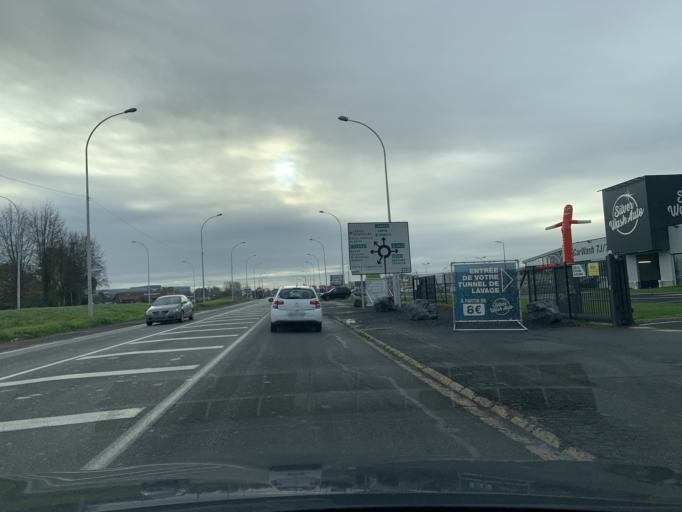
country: FR
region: Nord-Pas-de-Calais
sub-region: Departement du Nord
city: Dechy
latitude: 50.3431
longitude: 3.0939
